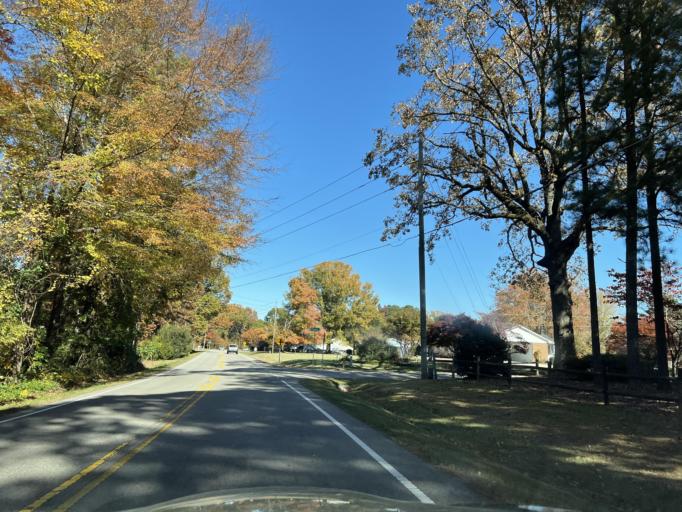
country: US
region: North Carolina
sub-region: Wake County
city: Garner
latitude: 35.6835
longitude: -78.6966
